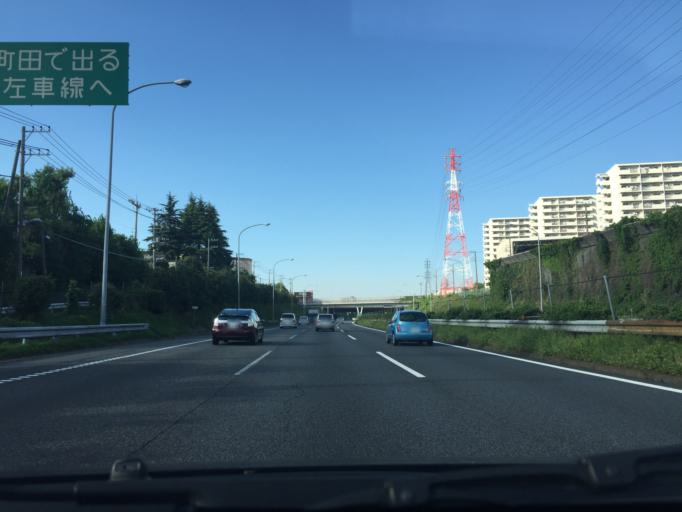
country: JP
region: Kanagawa
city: Minami-rinkan
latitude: 35.4953
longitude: 139.4733
